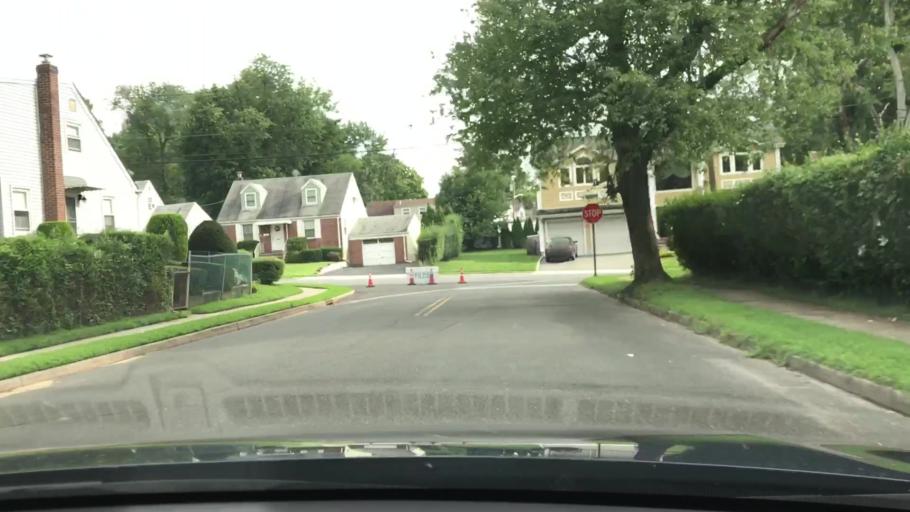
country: US
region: New Jersey
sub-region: Bergen County
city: Bergenfield
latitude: 40.9195
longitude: -74.0111
